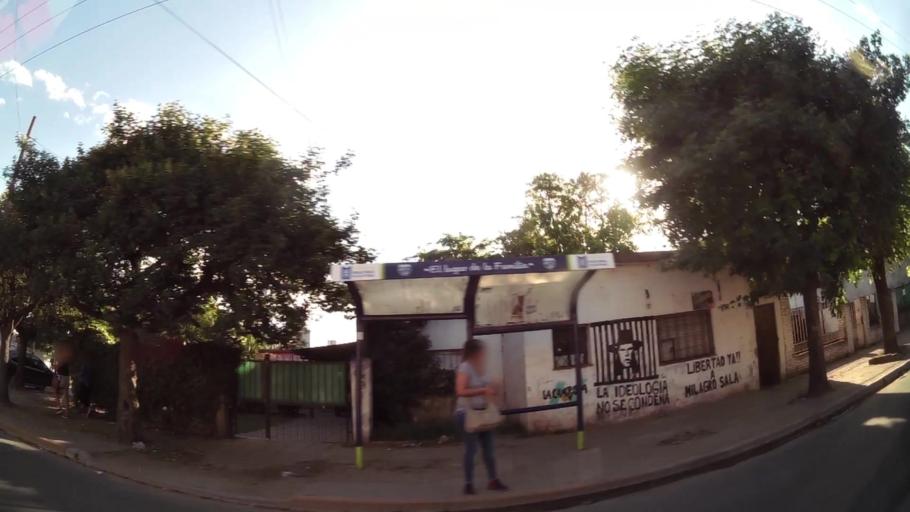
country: AR
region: Buenos Aires
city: Santa Catalina - Dique Lujan
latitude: -34.4958
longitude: -58.7192
